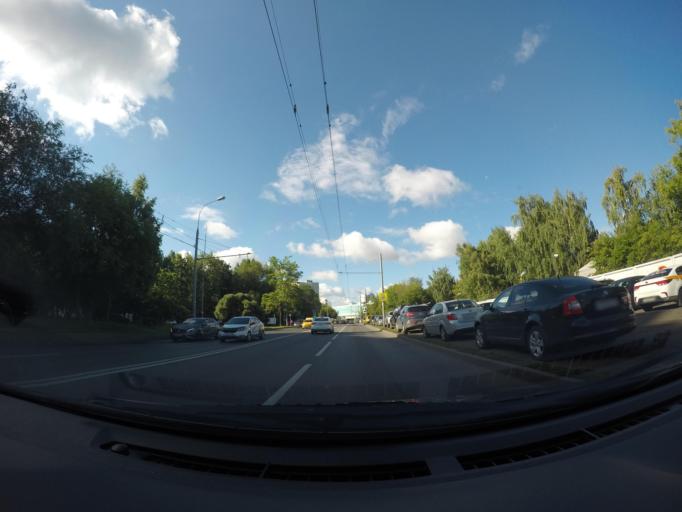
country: RU
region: Moscow
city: Khimki
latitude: 55.8667
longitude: 37.4378
